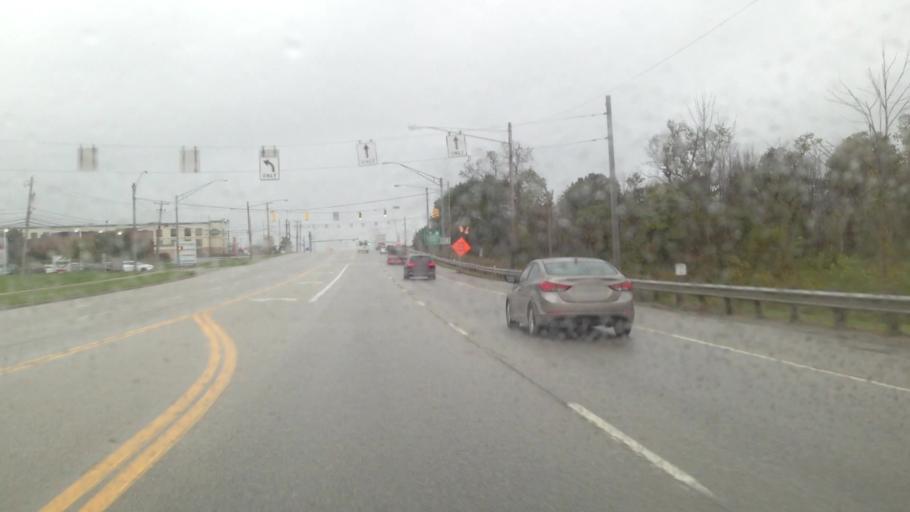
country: US
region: Ohio
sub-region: Portage County
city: Streetsboro
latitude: 41.2478
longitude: -81.3606
